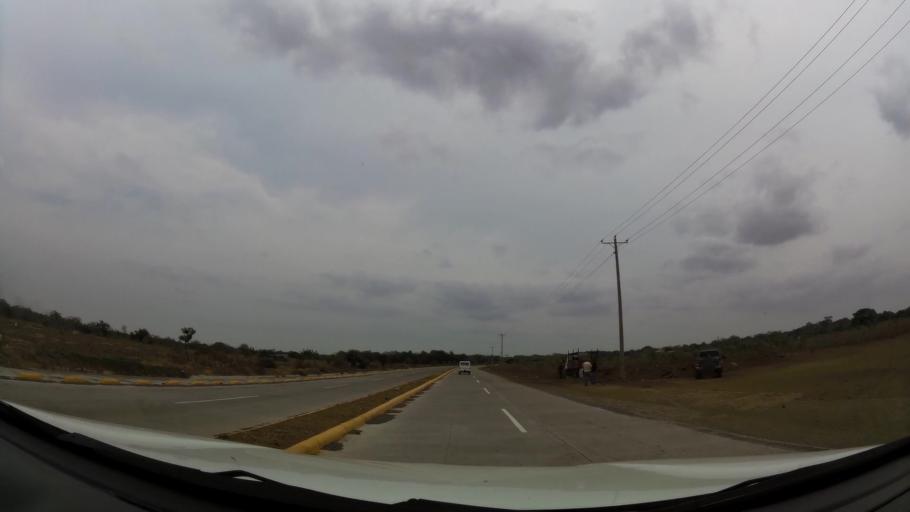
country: NI
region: Managua
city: Managua
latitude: 12.1128
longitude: -86.1729
